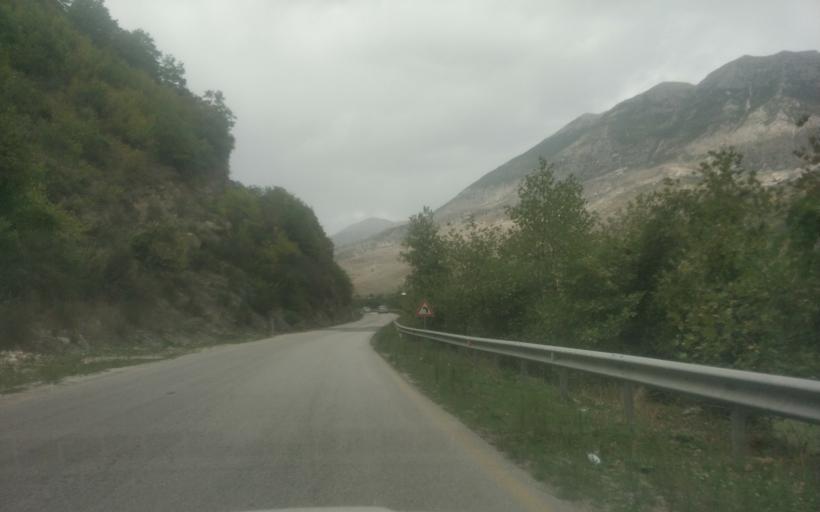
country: AL
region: Gjirokaster
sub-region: Rrethi i Gjirokastres
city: Picar
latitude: 40.2273
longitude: 20.0854
